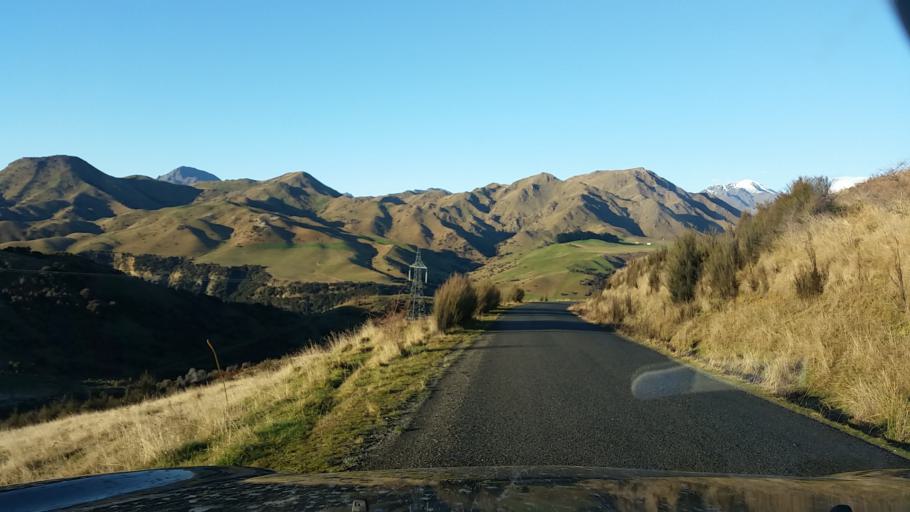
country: NZ
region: Marlborough
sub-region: Marlborough District
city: Blenheim
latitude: -41.7960
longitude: 173.7803
